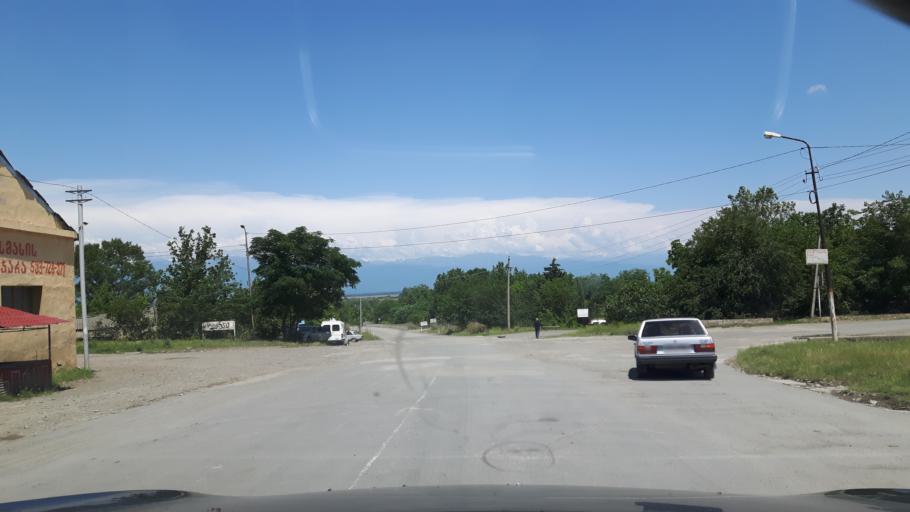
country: GE
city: Tsnori
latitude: 41.6143
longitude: 45.9934
